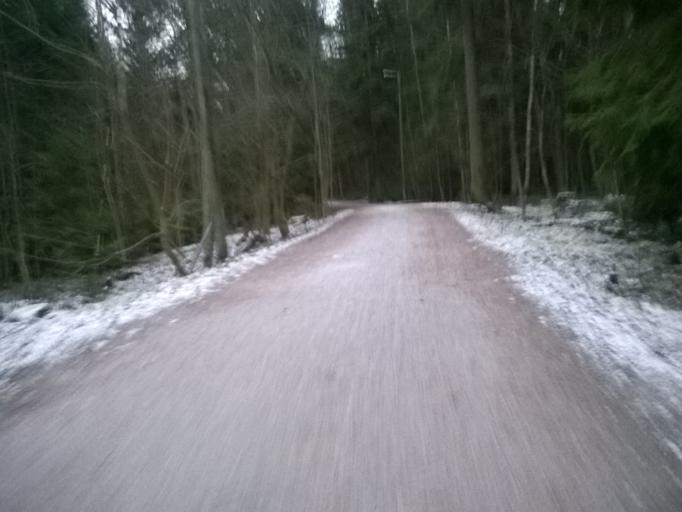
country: FI
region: Uusimaa
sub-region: Helsinki
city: Helsinki
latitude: 60.2552
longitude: 24.9016
